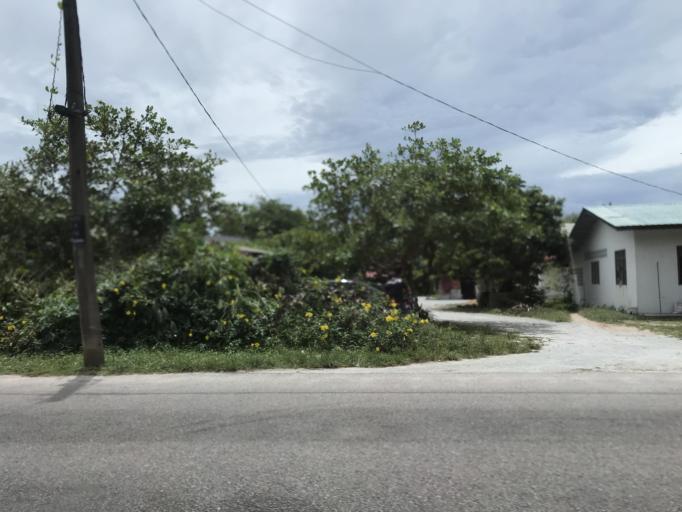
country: MY
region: Kelantan
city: Tumpat
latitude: 6.1785
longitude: 102.1834
